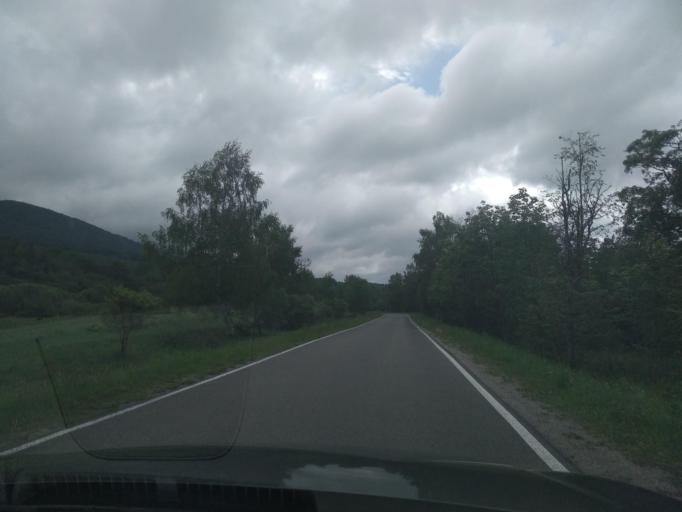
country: PL
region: Subcarpathian Voivodeship
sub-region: Powiat bieszczadzki
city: Lutowiska
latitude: 49.0774
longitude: 22.6634
